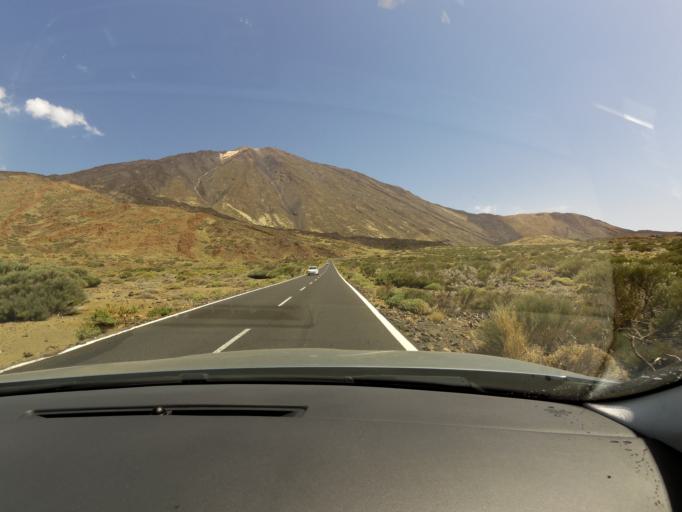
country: ES
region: Canary Islands
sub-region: Provincia de Santa Cruz de Tenerife
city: Vilaflor
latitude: 28.2394
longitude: -16.6299
